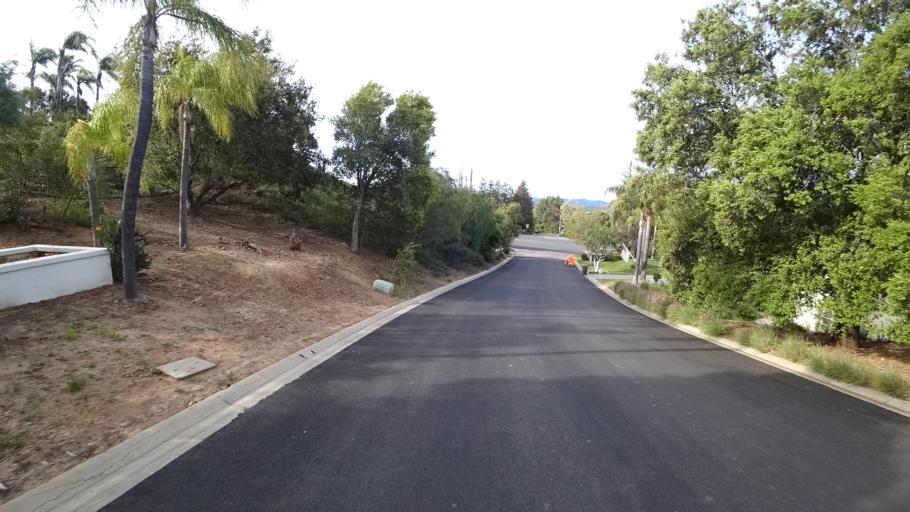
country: US
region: California
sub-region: Ventura County
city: Thousand Oaks
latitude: 34.1973
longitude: -118.8089
